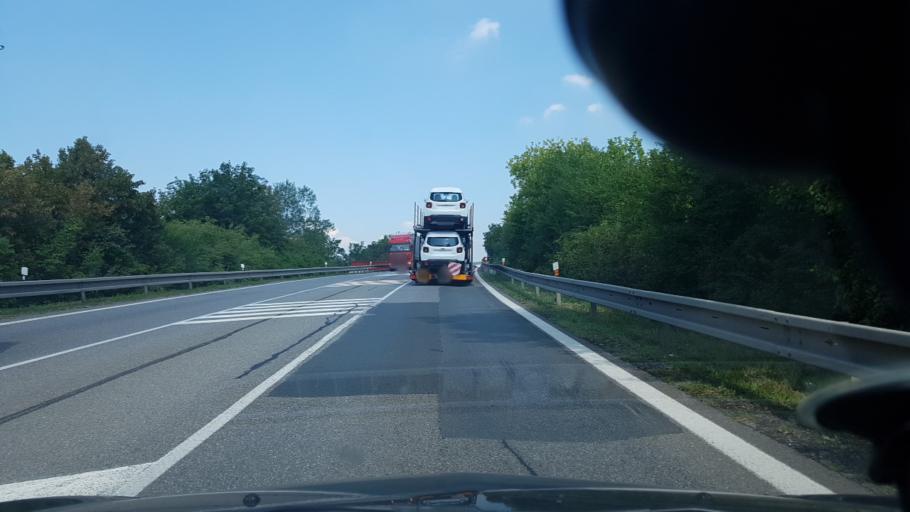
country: CZ
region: South Moravian
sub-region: Okres Breclav
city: Mikulov
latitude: 48.7925
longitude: 16.6341
